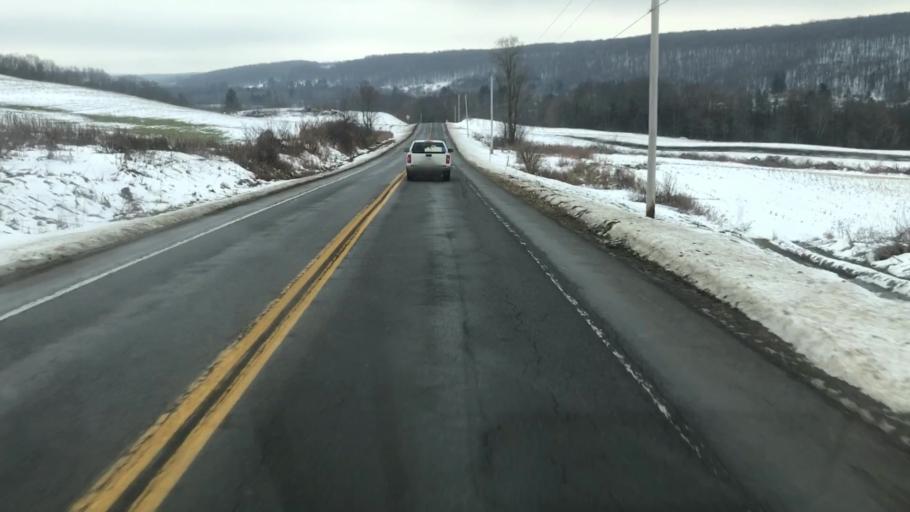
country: US
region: New York
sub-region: Tompkins County
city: Groton
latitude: 42.6870
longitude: -76.3013
